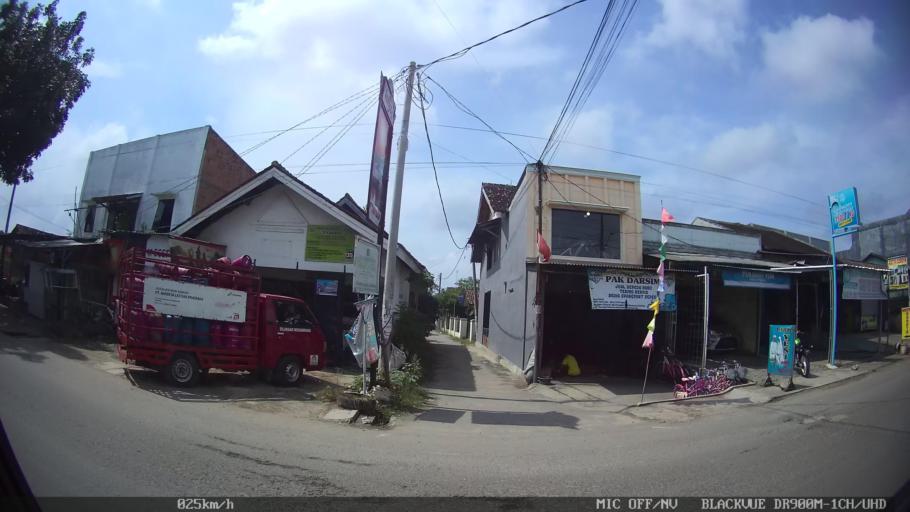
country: ID
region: Lampung
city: Kedaton
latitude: -5.3626
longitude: 105.2814
